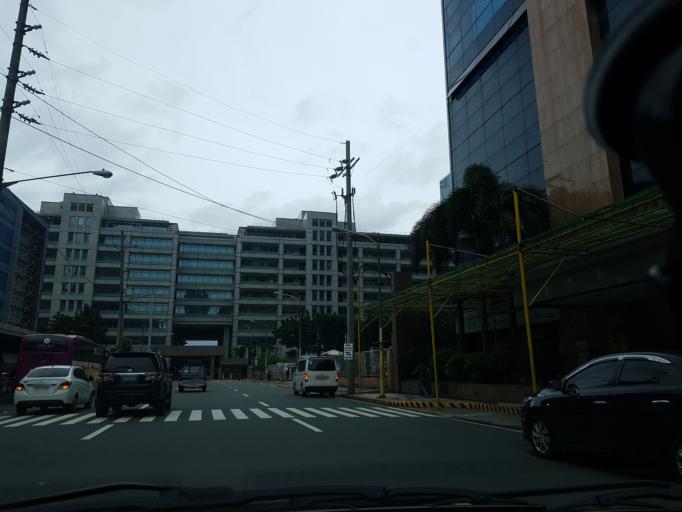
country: PH
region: Metro Manila
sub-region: Pasig
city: Pasig City
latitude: 14.5859
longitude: 121.0579
